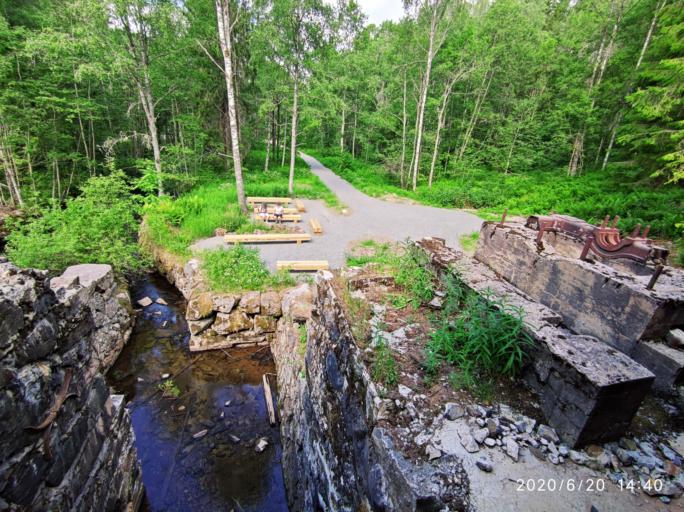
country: NO
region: Akershus
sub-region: Lorenskog
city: Kjenn
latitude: 59.8777
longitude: 10.9898
